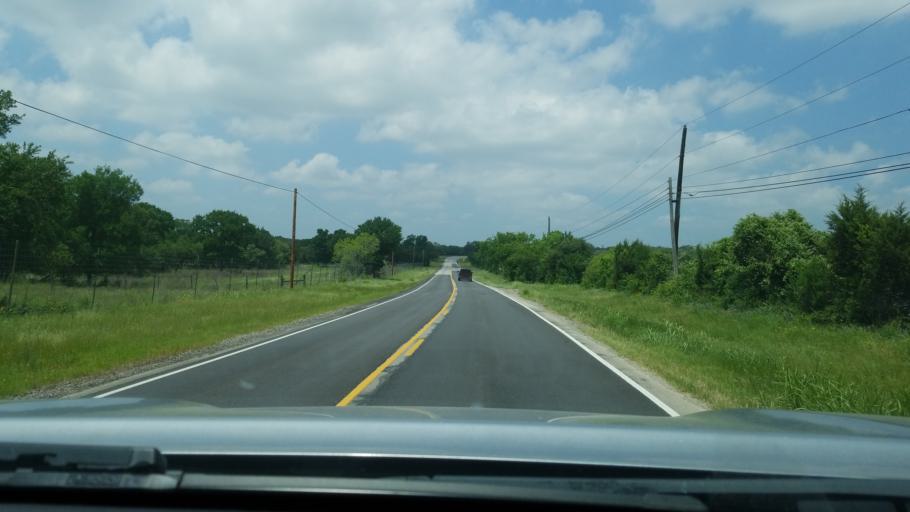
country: US
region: Texas
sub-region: Hays County
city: Dripping Springs
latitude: 30.1511
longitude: -98.0621
